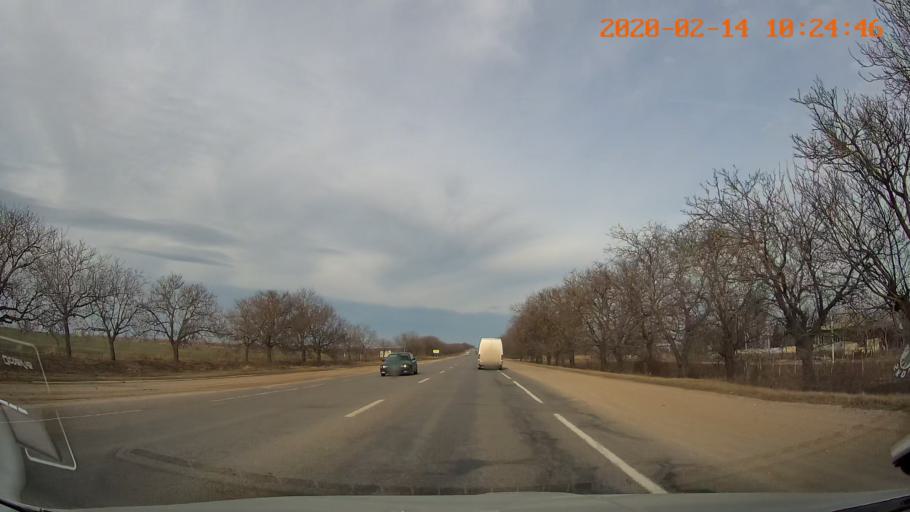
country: MD
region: Balti
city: Balti
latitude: 47.8268
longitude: 27.8177
